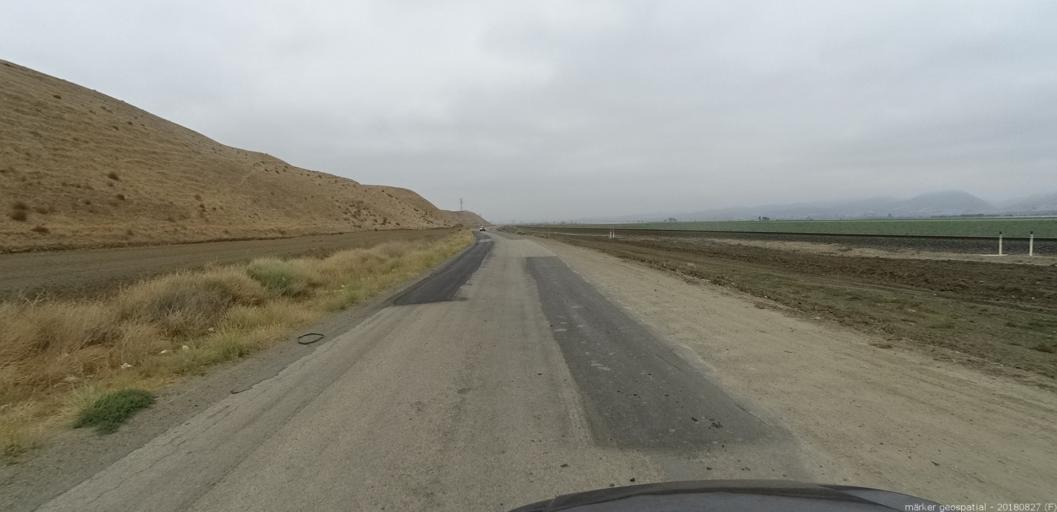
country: US
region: California
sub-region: Monterey County
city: King City
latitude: 36.2799
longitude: -121.1487
